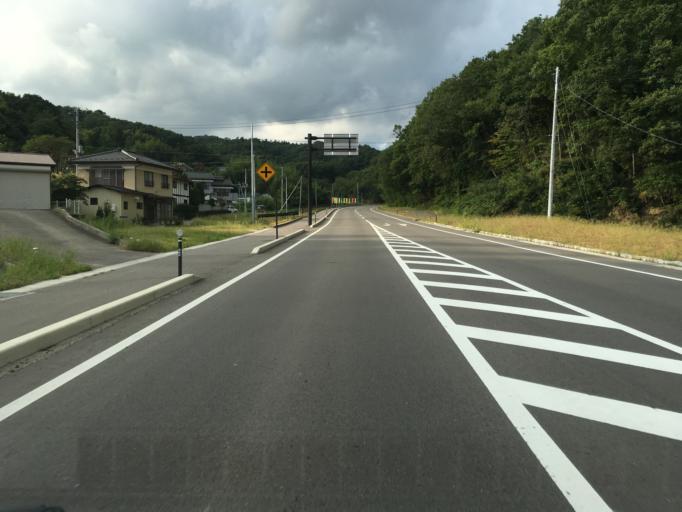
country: JP
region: Fukushima
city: Hobaramachi
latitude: 37.7316
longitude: 140.6040
